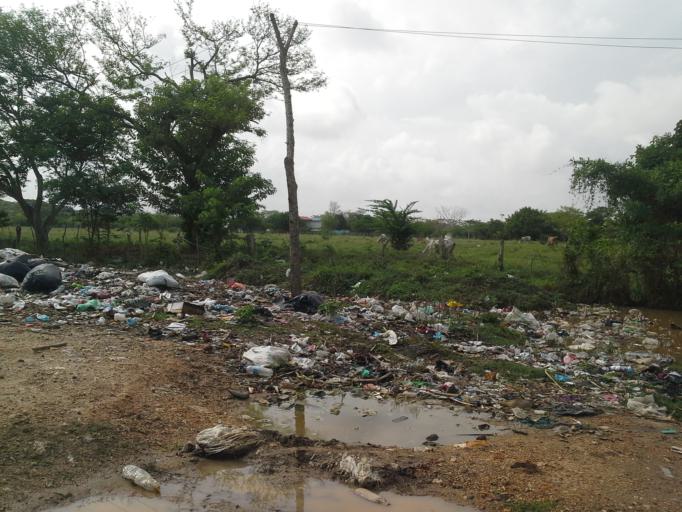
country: CO
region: Cordoba
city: Chima
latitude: 9.1035
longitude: -75.6213
